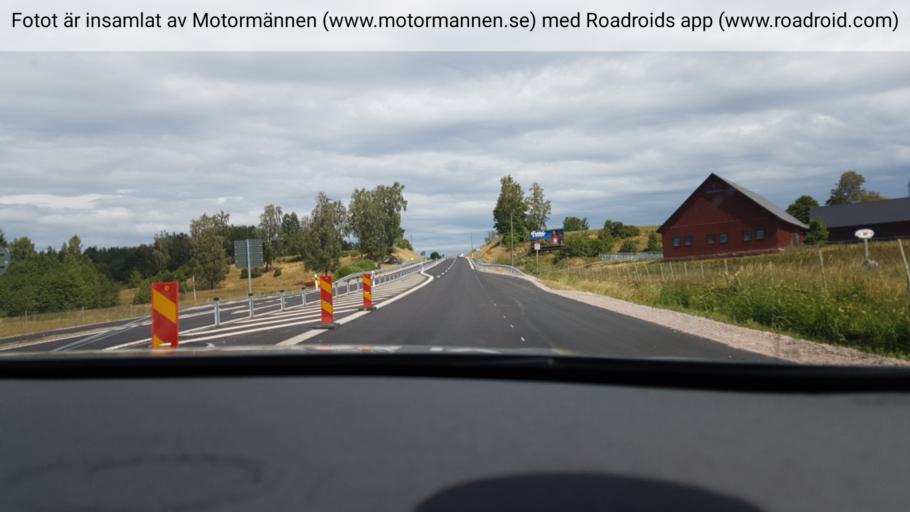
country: SE
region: Joenkoeping
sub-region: Tranas Kommun
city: Tranas
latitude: 58.0073
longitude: 14.9277
